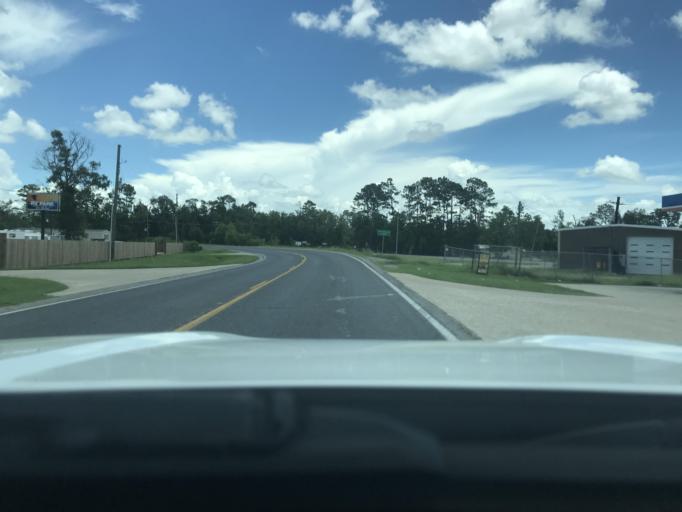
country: US
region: Louisiana
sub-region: Calcasieu Parish
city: Moss Bluff
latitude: 30.2771
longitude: -93.1708
